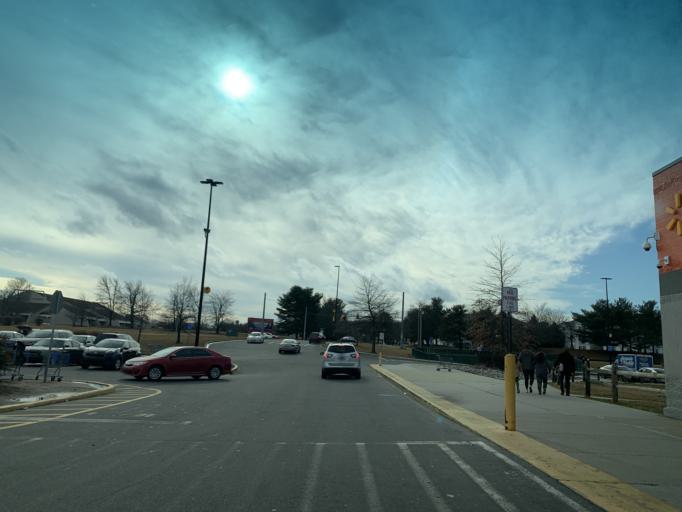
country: US
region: Delaware
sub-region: New Castle County
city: Bear
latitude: 39.6529
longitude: -75.6221
